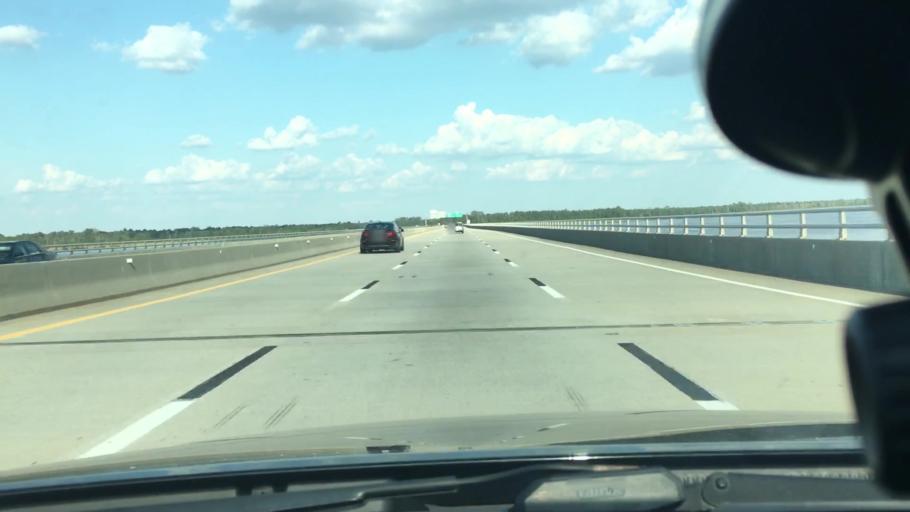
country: US
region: North Carolina
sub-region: Craven County
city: James City
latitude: 35.0975
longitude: -77.0247
